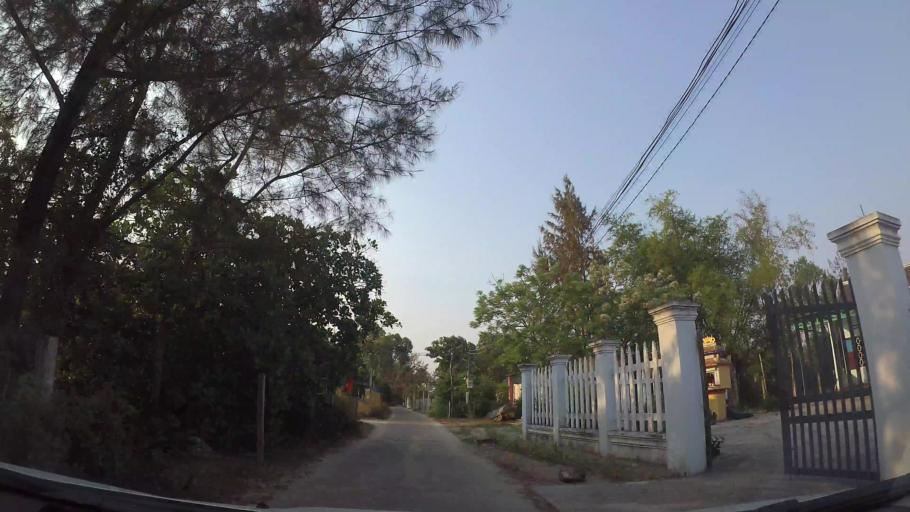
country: VN
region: Da Nang
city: Ngu Hanh Son
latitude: 15.9694
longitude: 108.2445
